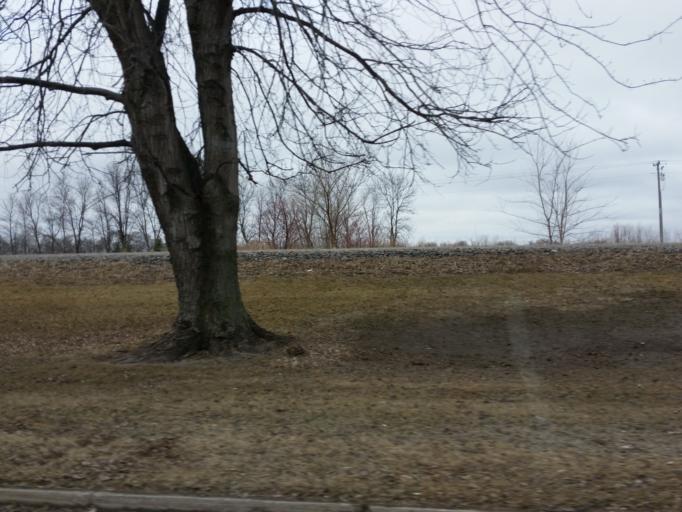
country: US
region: North Dakota
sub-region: Cass County
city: Casselton
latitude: 47.1063
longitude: -97.2182
